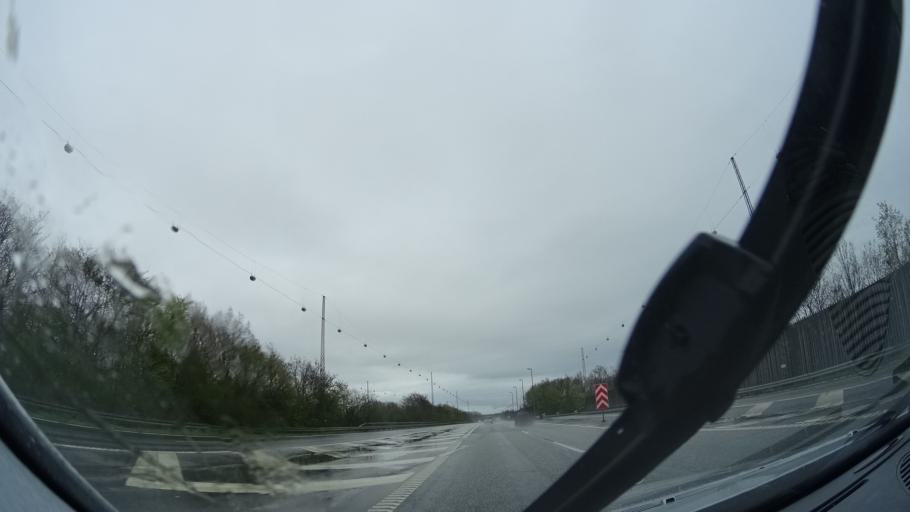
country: DK
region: Capital Region
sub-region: Hoje-Taastrup Kommune
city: Taastrup
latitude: 55.6601
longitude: 12.3141
